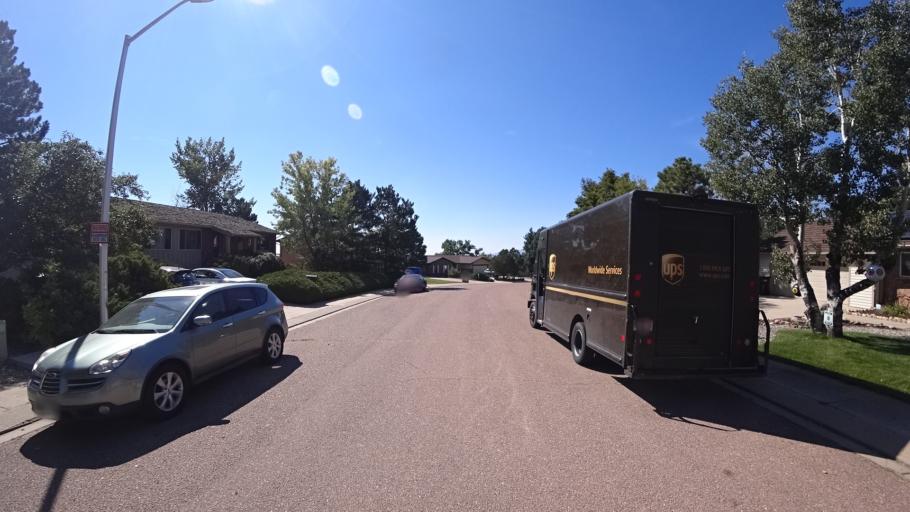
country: US
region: Colorado
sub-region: El Paso County
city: Cimarron Hills
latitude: 38.9137
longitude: -104.7632
